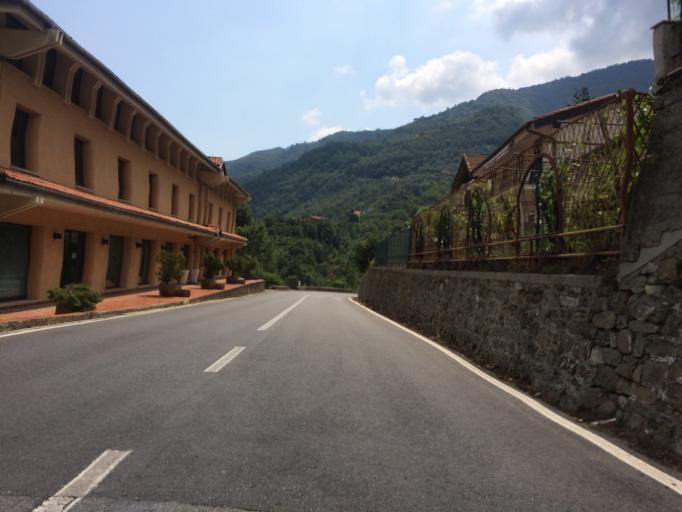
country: IT
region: Liguria
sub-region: Provincia di Imperia
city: Pigna
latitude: 43.9281
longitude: 7.6492
